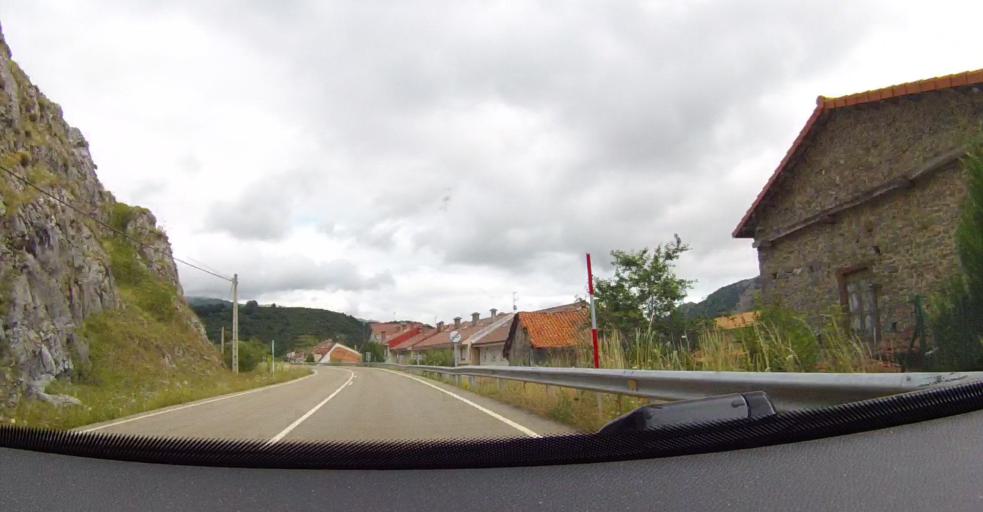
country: ES
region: Castille and Leon
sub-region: Provincia de Leon
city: Buron
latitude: 43.0254
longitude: -5.0548
